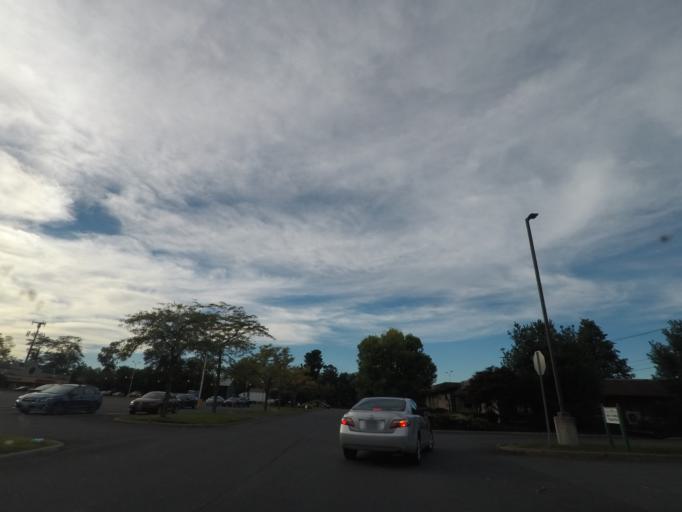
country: US
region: New York
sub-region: Rensselaer County
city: East Greenbush
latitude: 42.5977
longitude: -73.7100
